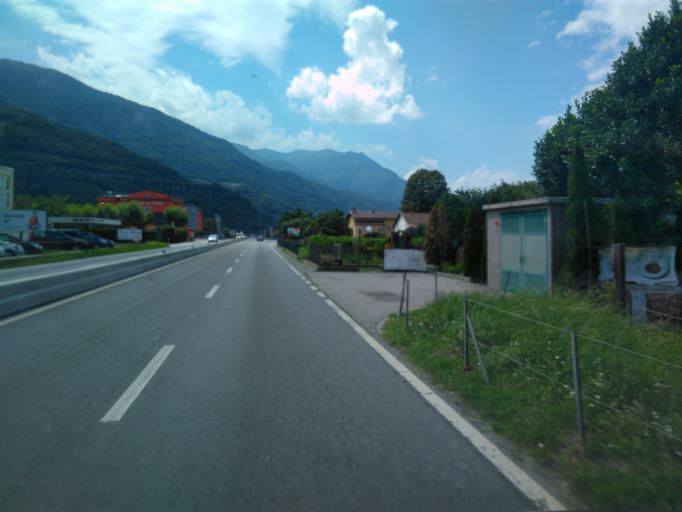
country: CH
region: Ticino
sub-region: Bellinzona District
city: Camorino
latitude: 46.1581
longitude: 8.9777
